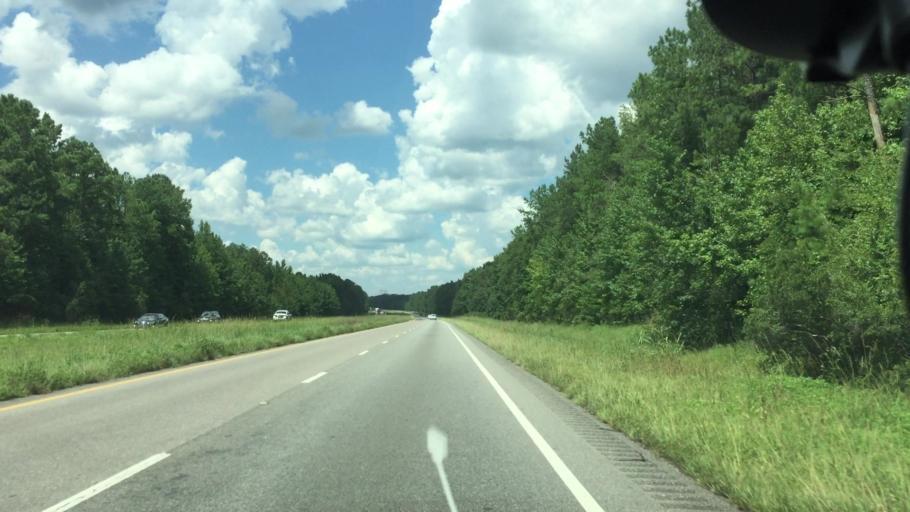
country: US
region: Alabama
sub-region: Pike County
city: Troy
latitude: 31.9873
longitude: -86.0267
